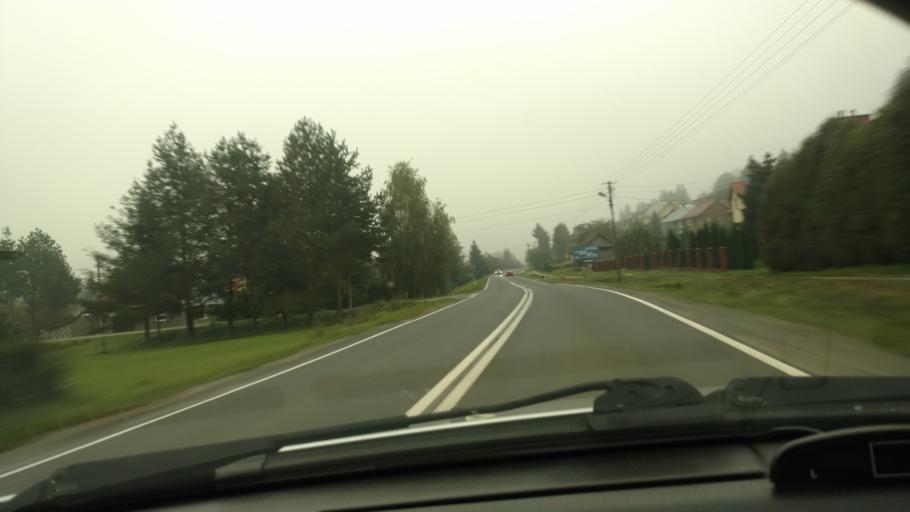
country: PL
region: Subcarpathian Voivodeship
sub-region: Powiat strzyzowski
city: Frysztak
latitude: 49.8286
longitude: 21.6185
